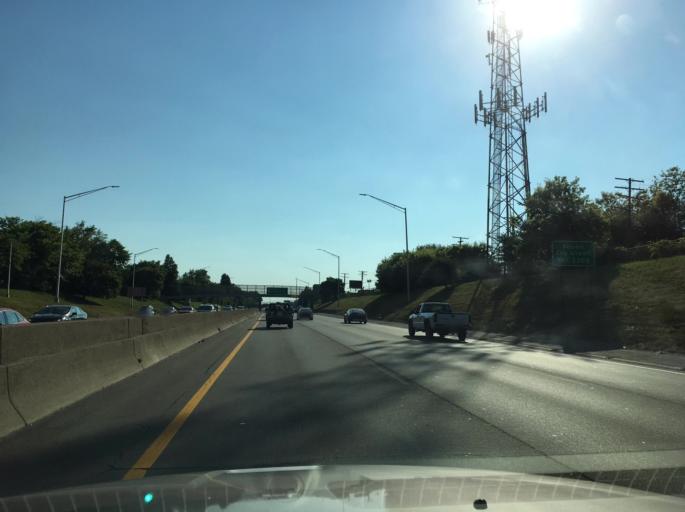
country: US
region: Michigan
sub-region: Wayne County
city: Grosse Pointe Park
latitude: 42.4029
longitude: -82.9679
